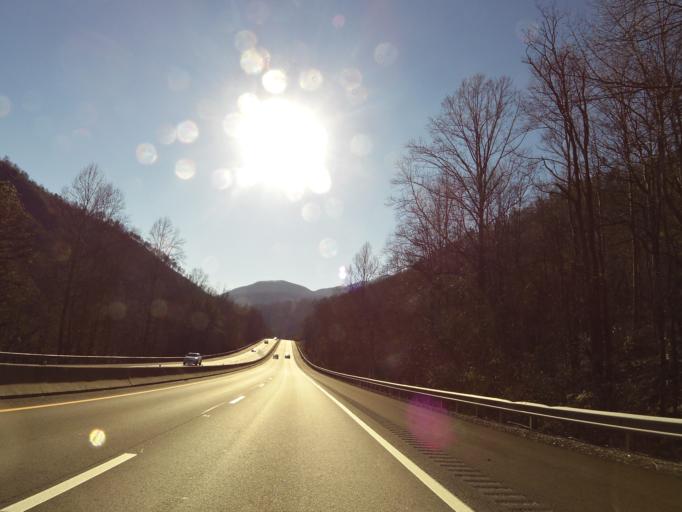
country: US
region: Tennessee
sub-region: Cocke County
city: Newport
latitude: 35.8208
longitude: -83.1821
